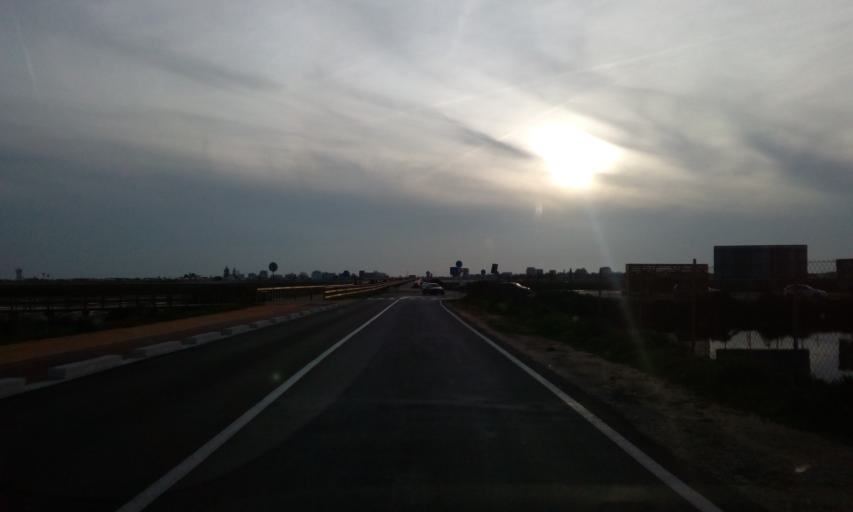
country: PT
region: Faro
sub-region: Faro
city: Faro
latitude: 37.0152
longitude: -7.9871
